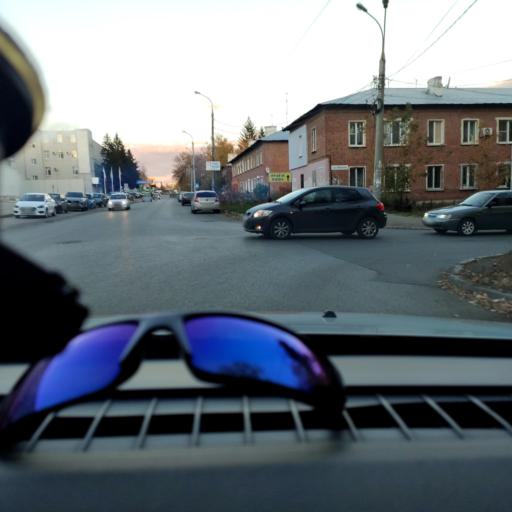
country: RU
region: Samara
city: Samara
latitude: 53.2370
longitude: 50.2437
